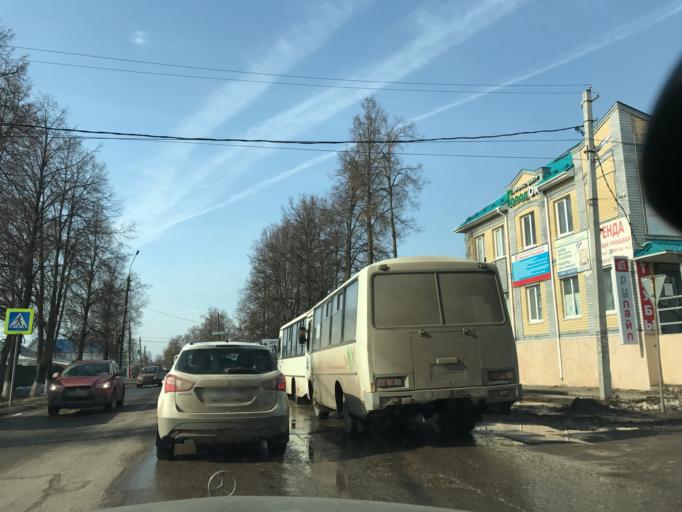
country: RU
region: Nizjnij Novgorod
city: Pavlovo
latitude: 55.9632
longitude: 43.0878
